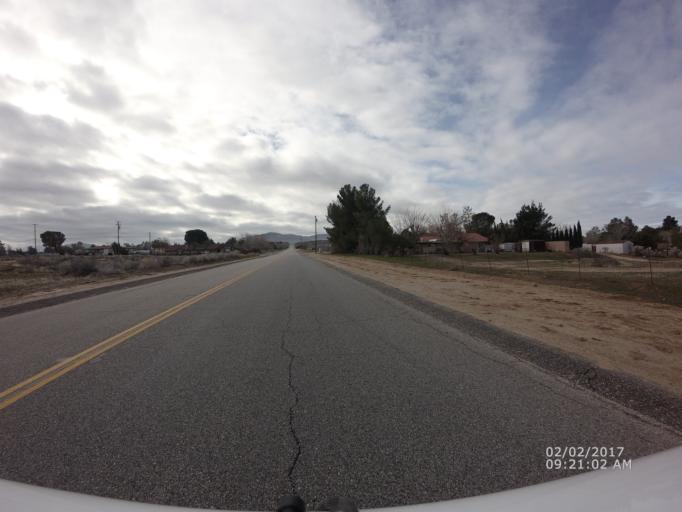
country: US
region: California
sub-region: Los Angeles County
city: Vincent
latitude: 34.5400
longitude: -118.0585
